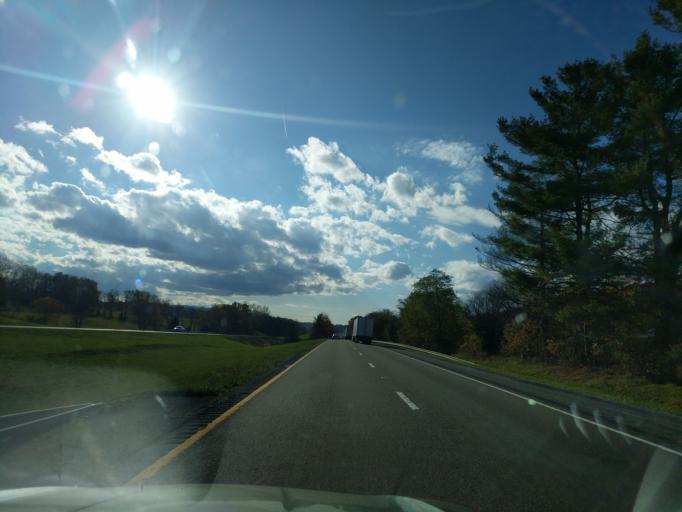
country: US
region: Virginia
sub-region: Wythe County
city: Wytheville
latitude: 36.9336
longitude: -81.1776
